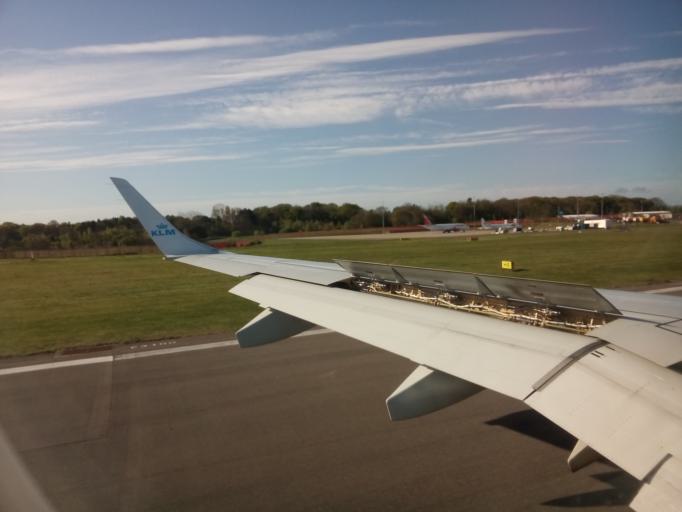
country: GB
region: England
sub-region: Newcastle upon Tyne
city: Dinnington
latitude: 55.0376
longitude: -1.6911
